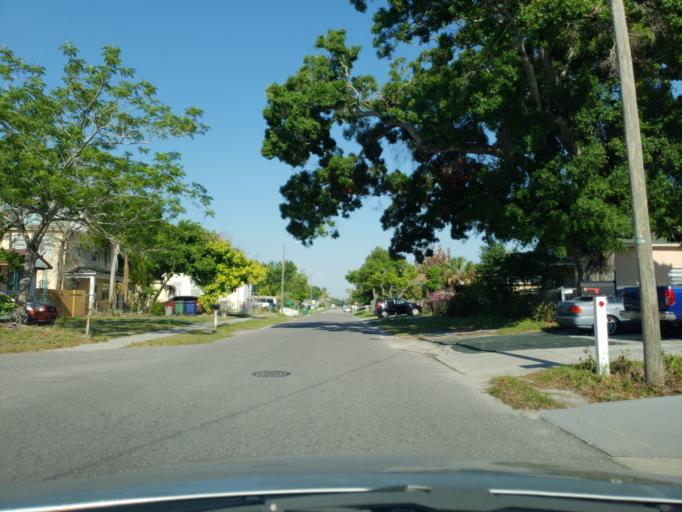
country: US
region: Florida
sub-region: Hillsborough County
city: Tampa
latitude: 27.9631
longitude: -82.4906
